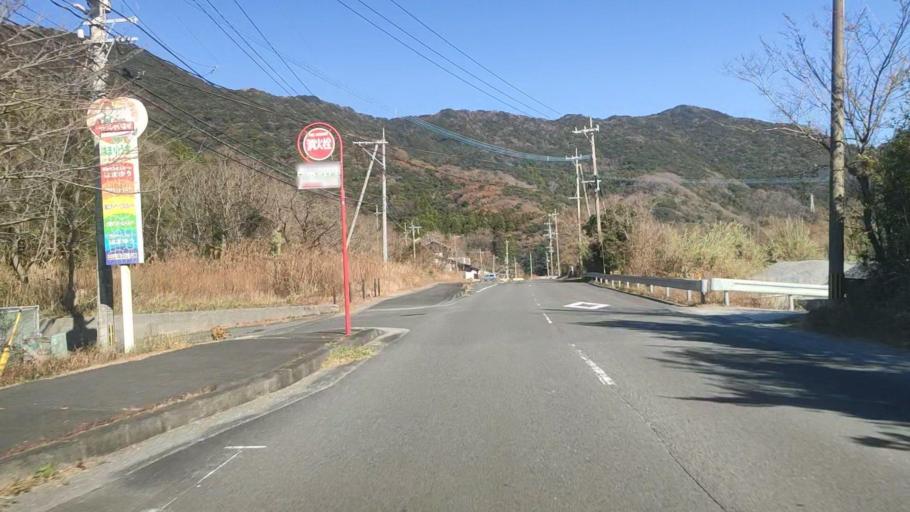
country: JP
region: Oita
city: Saiki
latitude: 32.8032
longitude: 131.9440
